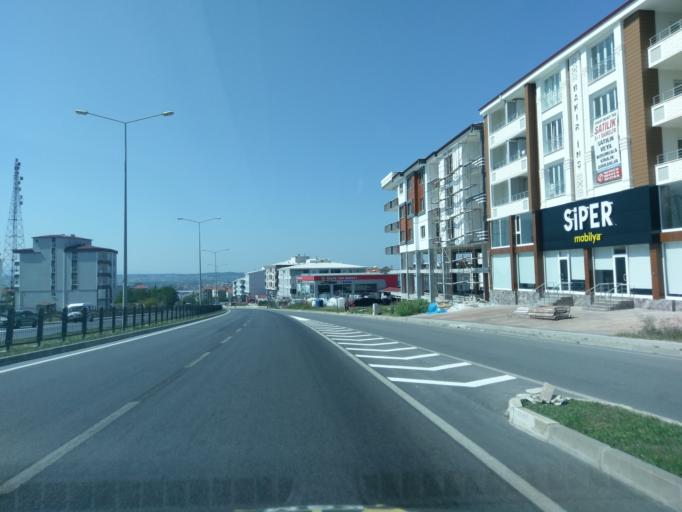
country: TR
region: Samsun
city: Bafra
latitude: 41.5543
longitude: 35.9212
